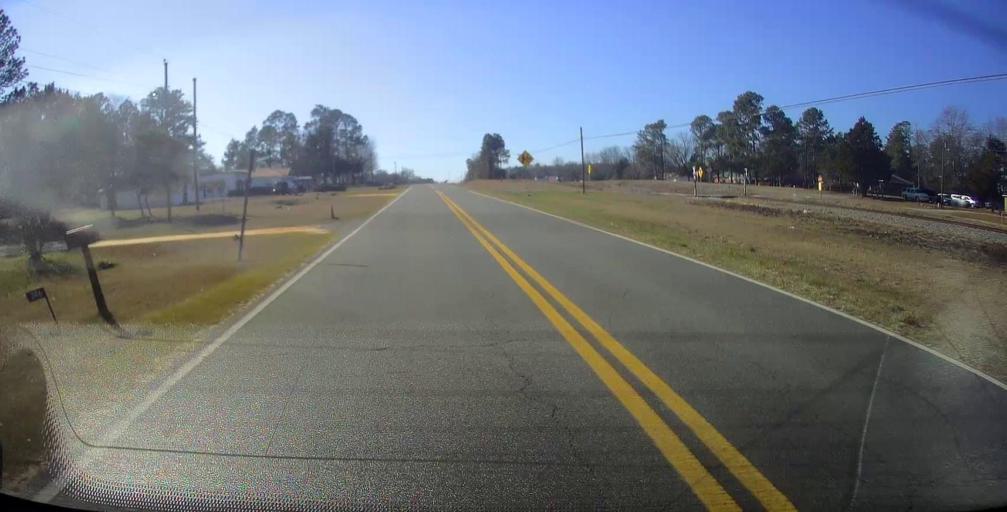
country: US
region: Georgia
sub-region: Taylor County
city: Butler
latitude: 32.5557
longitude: -84.2166
